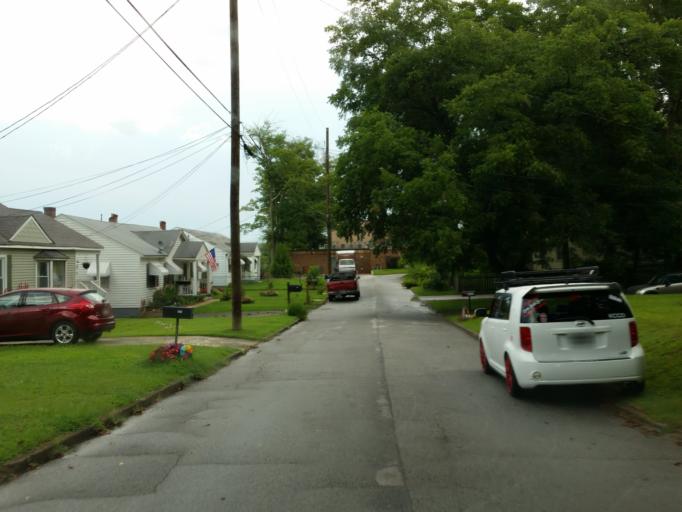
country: US
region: Georgia
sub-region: Cobb County
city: Marietta
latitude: 33.9427
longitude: -84.5425
